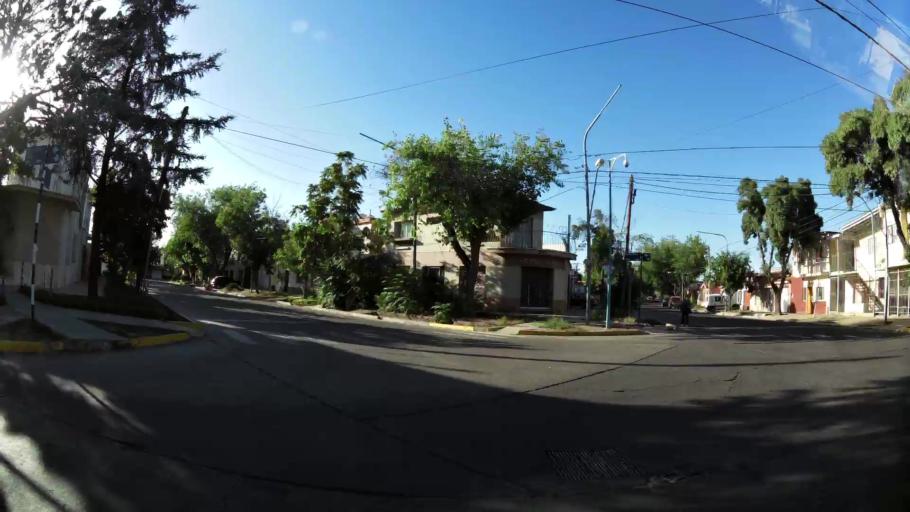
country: AR
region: Mendoza
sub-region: Departamento de Godoy Cruz
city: Godoy Cruz
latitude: -32.9411
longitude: -68.8460
